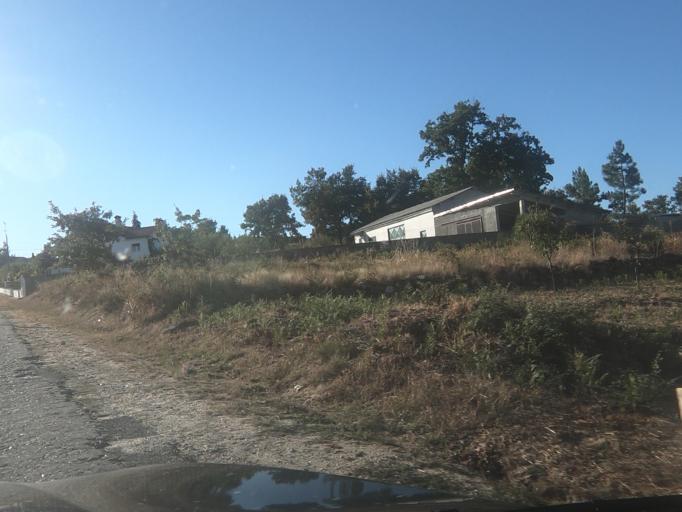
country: PT
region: Vila Real
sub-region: Sabrosa
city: Sabrosa
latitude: 41.3262
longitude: -7.6014
